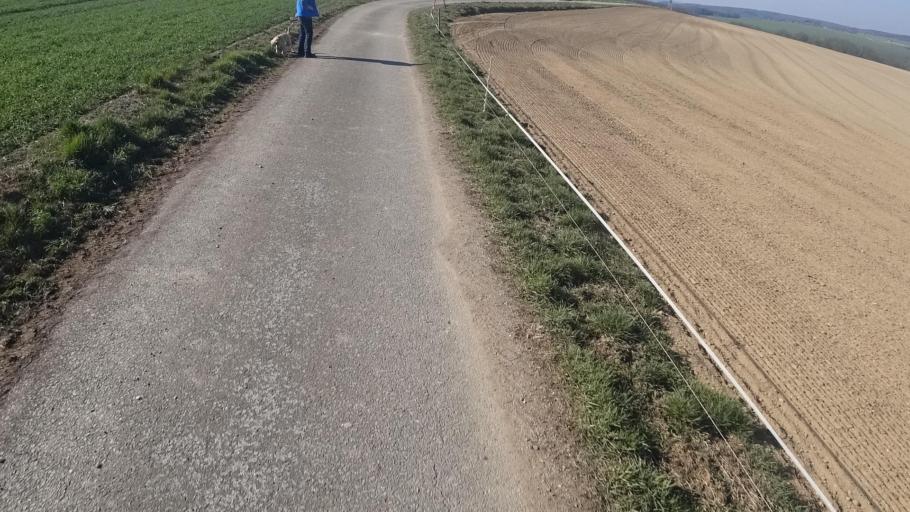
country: DE
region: Rheinland-Pfalz
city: Mengerschied
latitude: 49.9219
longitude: 7.4932
